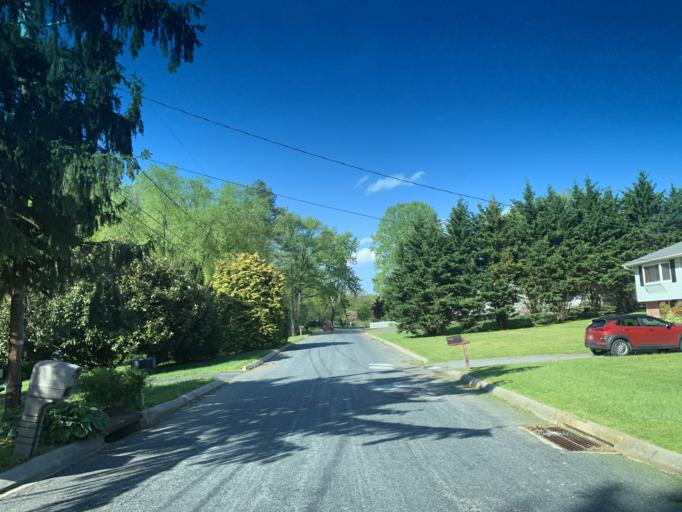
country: US
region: Maryland
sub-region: Harford County
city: Aberdeen
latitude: 39.5396
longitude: -76.2067
